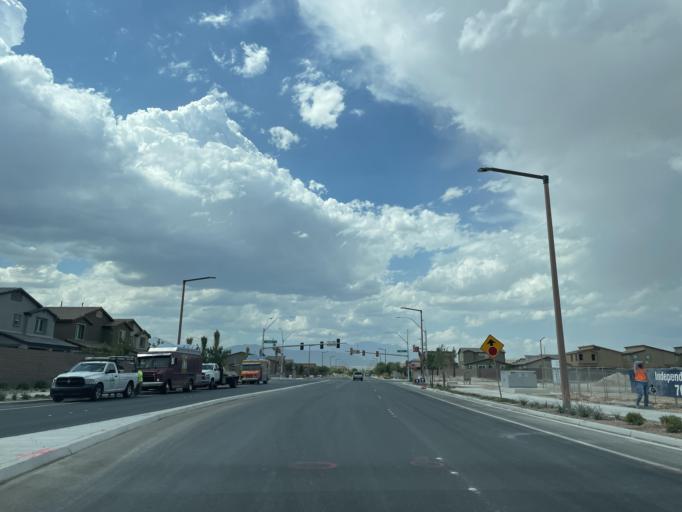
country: US
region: Nevada
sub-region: Clark County
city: North Las Vegas
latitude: 36.2988
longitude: -115.1970
